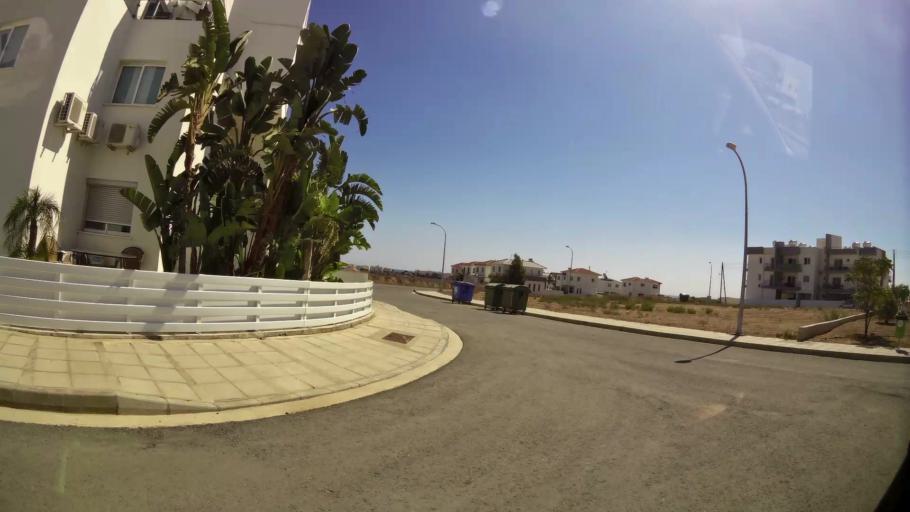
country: CY
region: Larnaka
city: Livadia
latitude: 34.9547
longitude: 33.6375
